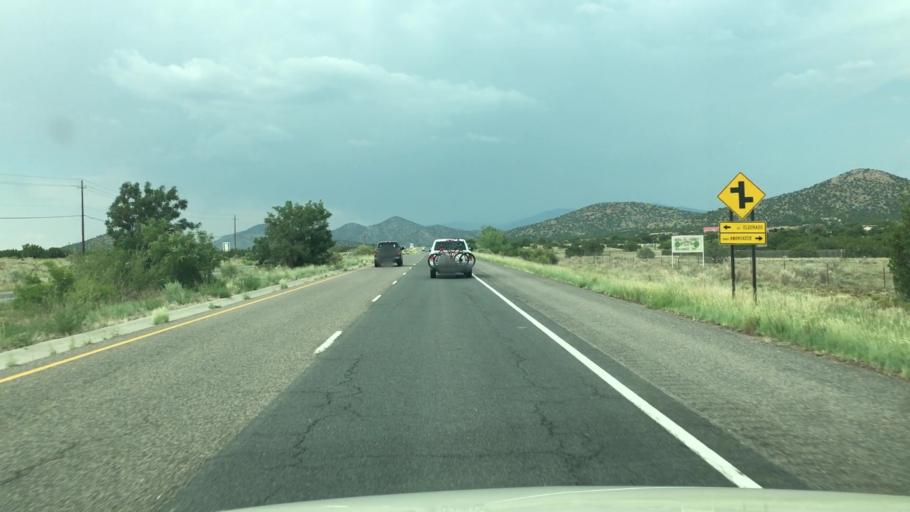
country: US
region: New Mexico
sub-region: Santa Fe County
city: Eldorado at Santa Fe
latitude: 35.5248
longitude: -105.8913
